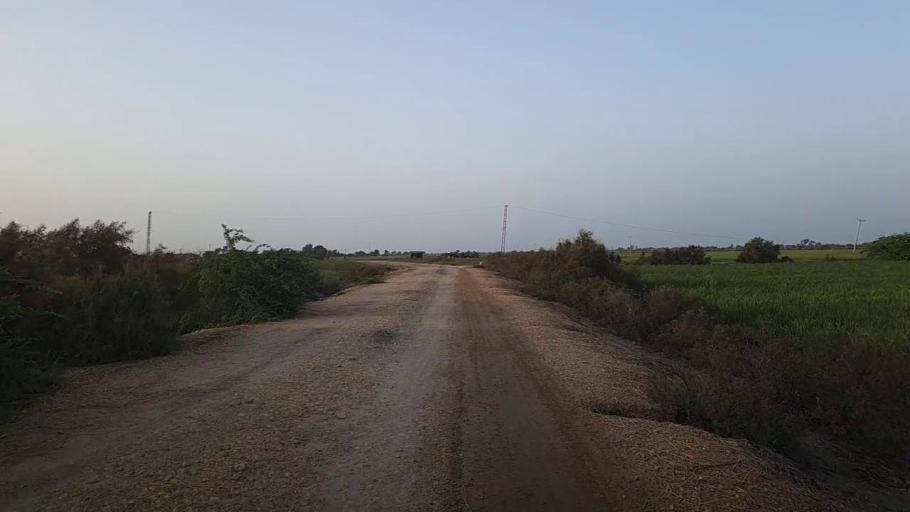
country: PK
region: Sindh
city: Kario
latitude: 24.7267
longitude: 68.4610
